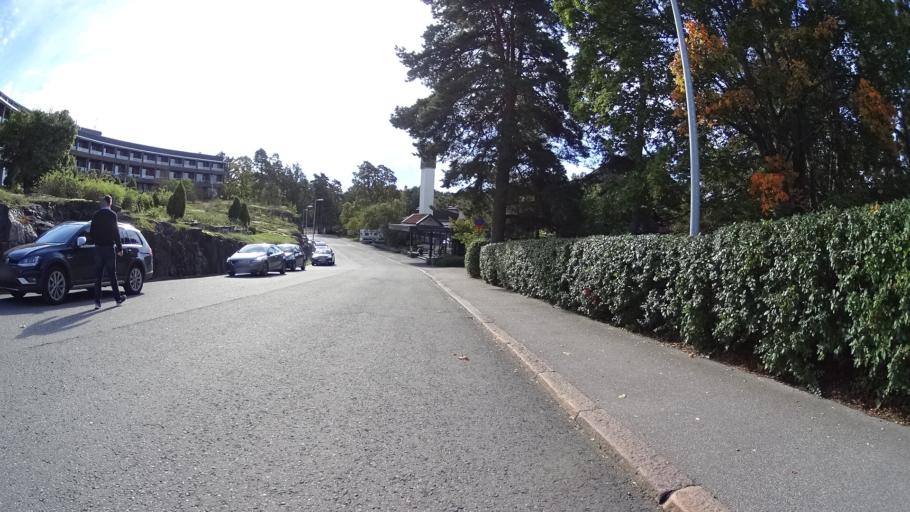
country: FI
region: Uusimaa
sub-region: Helsinki
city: Teekkarikylae
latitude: 60.1922
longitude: 24.8728
